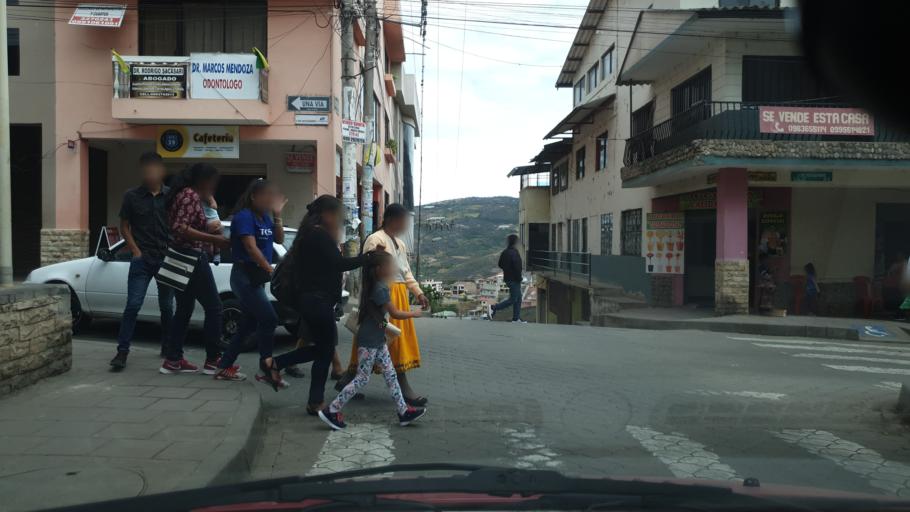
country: EC
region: Azuay
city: Cuenca
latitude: -3.2736
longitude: -79.3156
